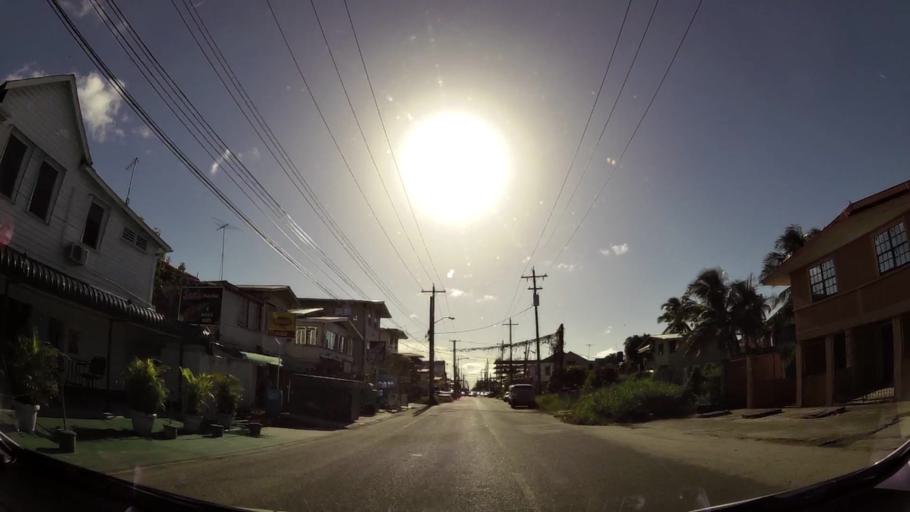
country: GY
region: Demerara-Mahaica
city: Georgetown
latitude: 6.8174
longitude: -58.1418
